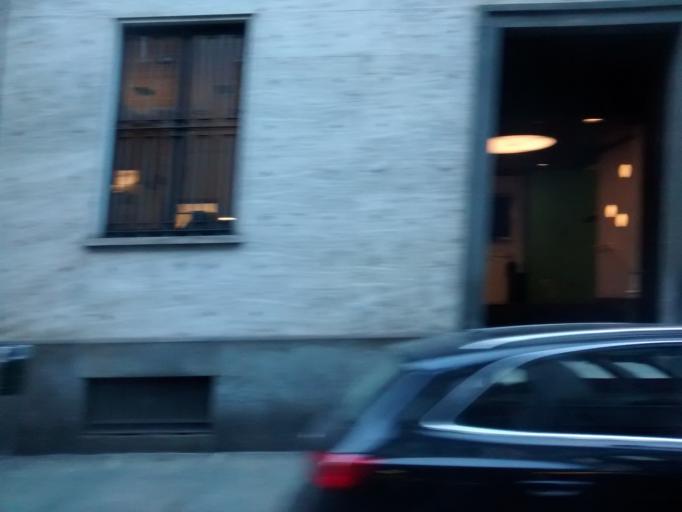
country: IT
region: Piedmont
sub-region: Provincia di Torino
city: Turin
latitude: 45.0689
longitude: 7.6803
